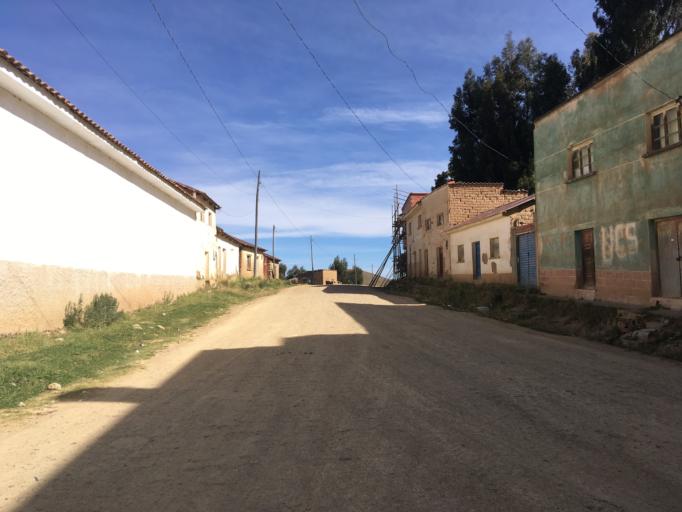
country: BO
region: La Paz
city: San Pedro
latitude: -16.2561
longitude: -68.8602
